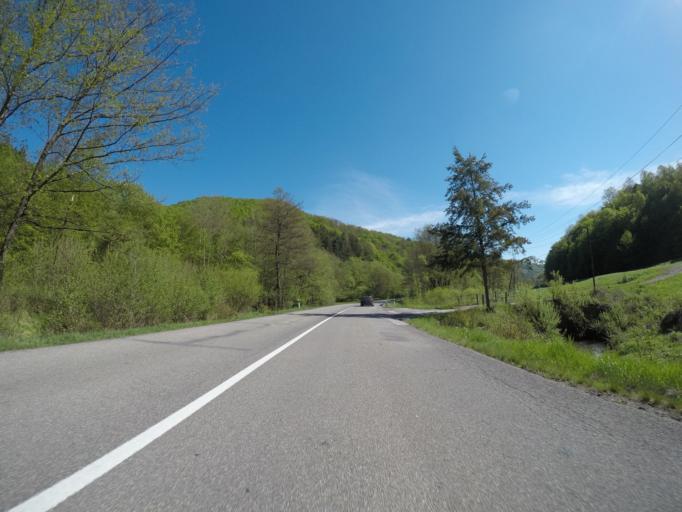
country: SK
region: Banskobystricky
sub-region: Okres Banska Bystrica
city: Banska Stiavnica
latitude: 48.5008
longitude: 18.9587
